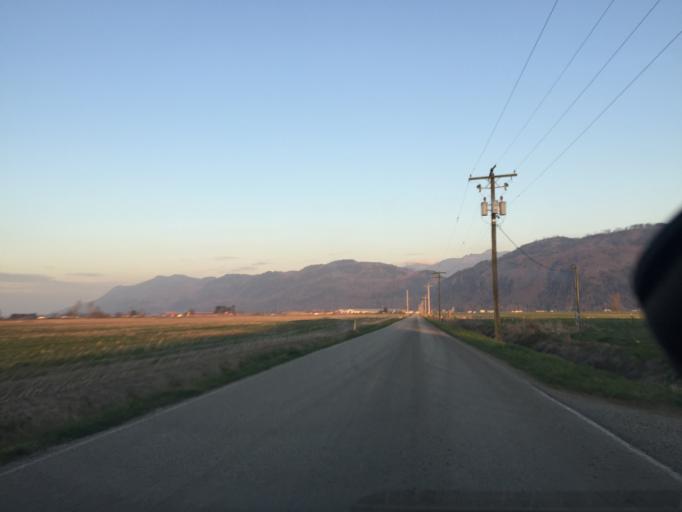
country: US
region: Washington
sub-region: Whatcom County
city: Sumas
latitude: 48.9999
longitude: -122.2153
